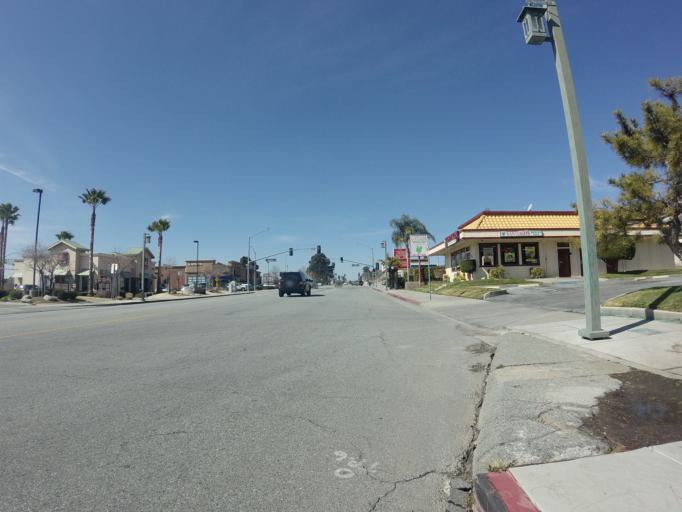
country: US
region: California
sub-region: Riverside County
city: Banning
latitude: 33.9255
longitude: -116.8846
